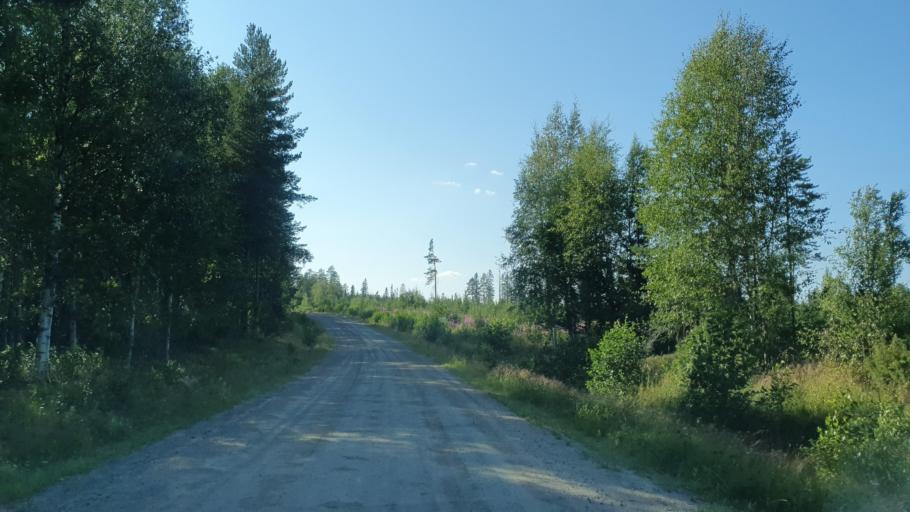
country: FI
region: Kainuu
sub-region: Kehys-Kainuu
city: Kuhmo
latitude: 64.0312
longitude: 29.6909
